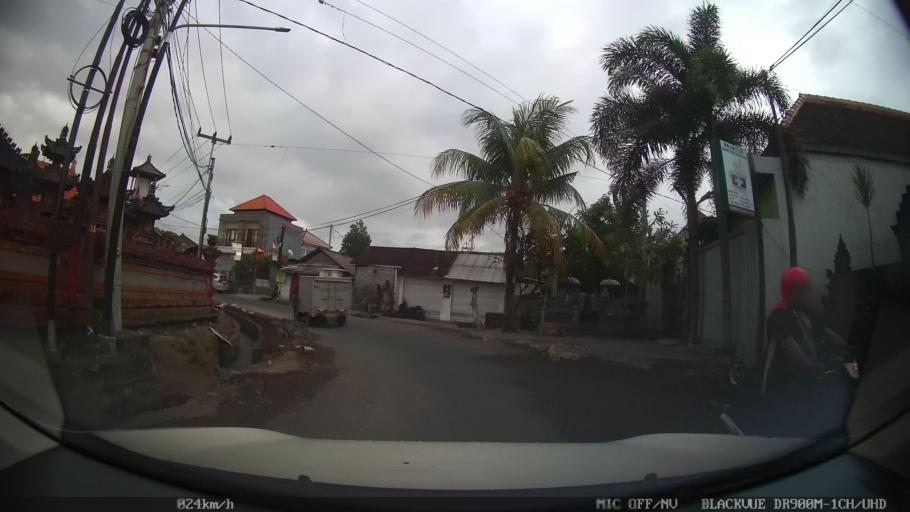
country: ID
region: Bali
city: Banjar Kertajiwa
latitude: -8.6358
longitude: 115.2646
